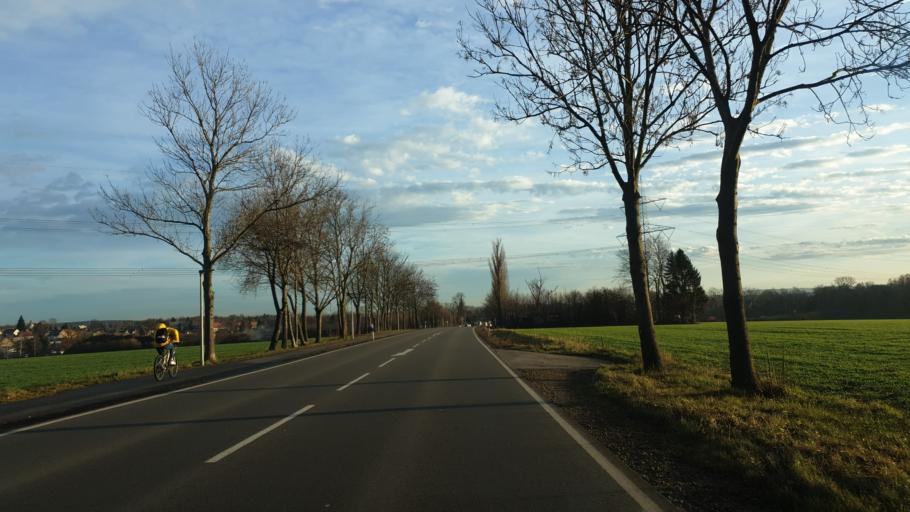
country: DE
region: Saxony
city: Neukirchen
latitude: 50.8078
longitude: 12.8138
